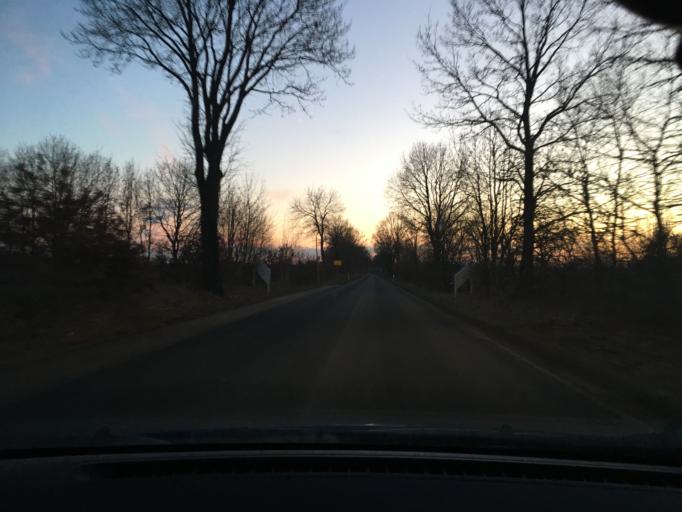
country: DE
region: Schleswig-Holstein
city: Fitzen
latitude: 53.4924
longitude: 10.6456
